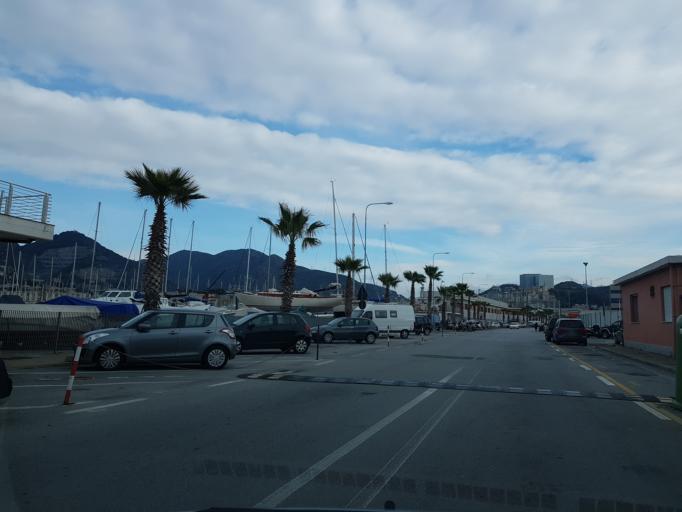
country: IT
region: Liguria
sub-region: Provincia di Genova
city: San Teodoro
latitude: 44.4154
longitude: 8.8435
